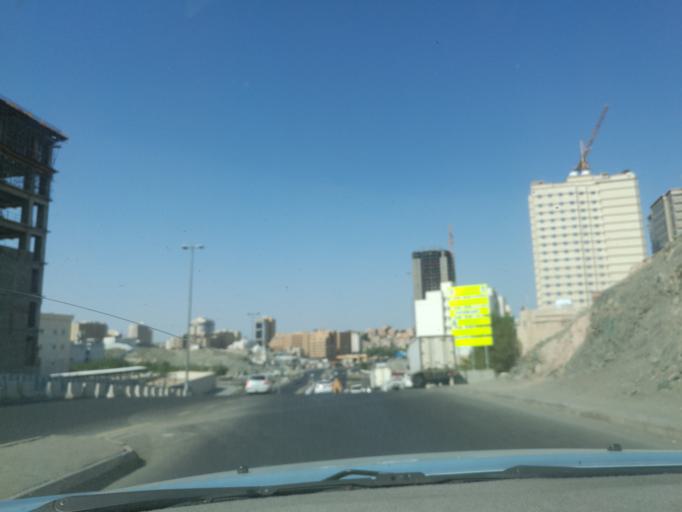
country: SA
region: Makkah
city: Mecca
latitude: 21.4340
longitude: 39.8140
